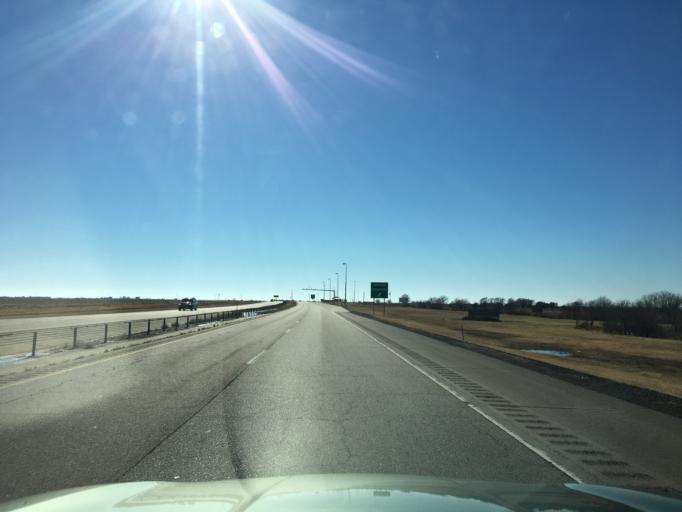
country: US
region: Oklahoma
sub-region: Kay County
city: Blackwell
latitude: 36.9930
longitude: -97.3445
